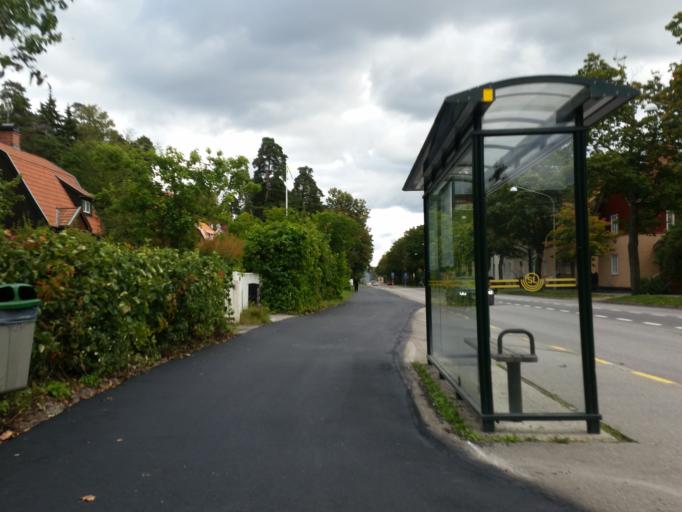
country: SE
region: Stockholm
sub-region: Stockholms Kommun
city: Arsta
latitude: 59.2841
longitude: 18.0996
